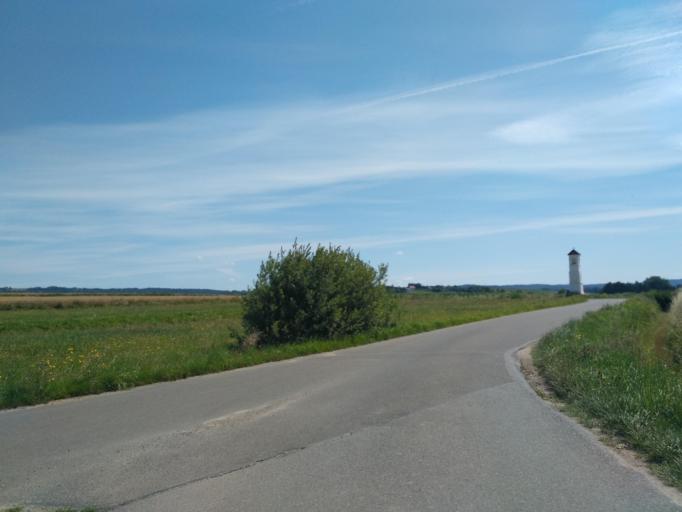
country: PL
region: Subcarpathian Voivodeship
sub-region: Powiat krosnienski
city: Kroscienko Wyzne
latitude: 49.6997
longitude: 21.8297
